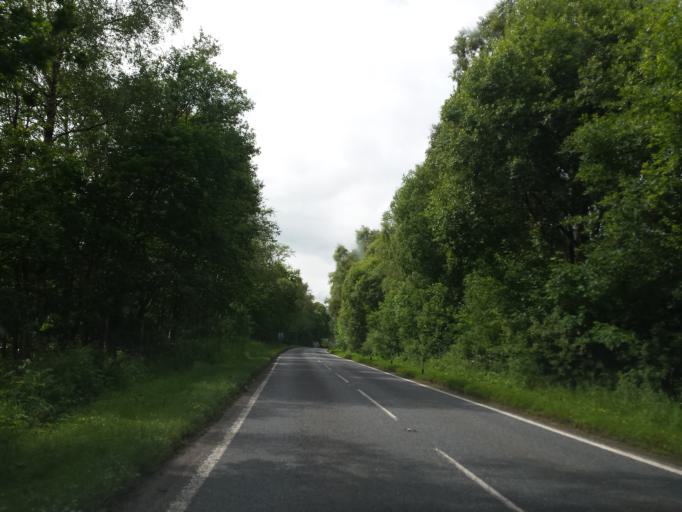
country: GB
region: Scotland
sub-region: Highland
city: Fort William
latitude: 56.8465
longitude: -5.1555
